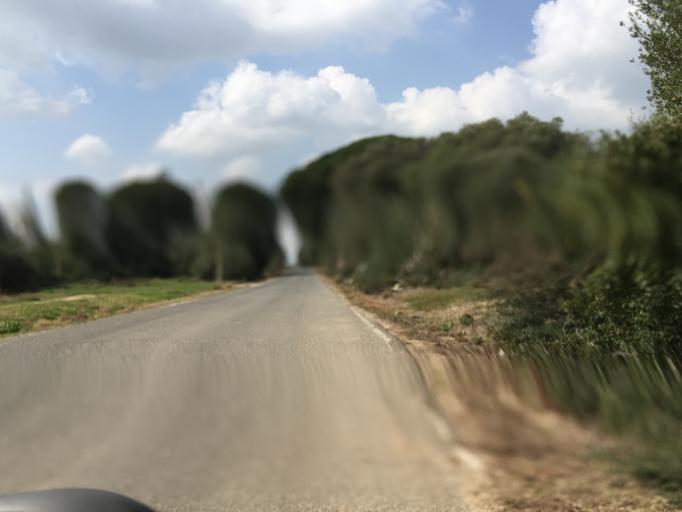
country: ES
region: Andalusia
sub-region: Provincia de Cadiz
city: Vejer de la Frontera
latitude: 36.2819
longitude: -5.9314
